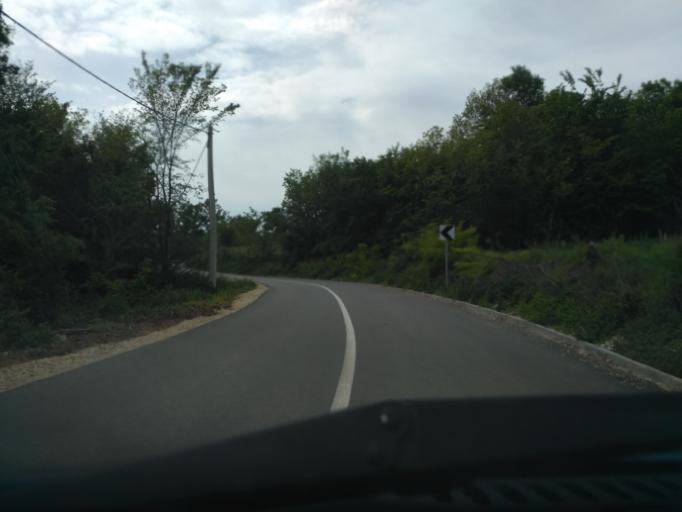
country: RS
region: Central Serbia
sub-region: Podunavski Okrug
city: Smederevska Palanka
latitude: 44.3575
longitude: 21.0066
